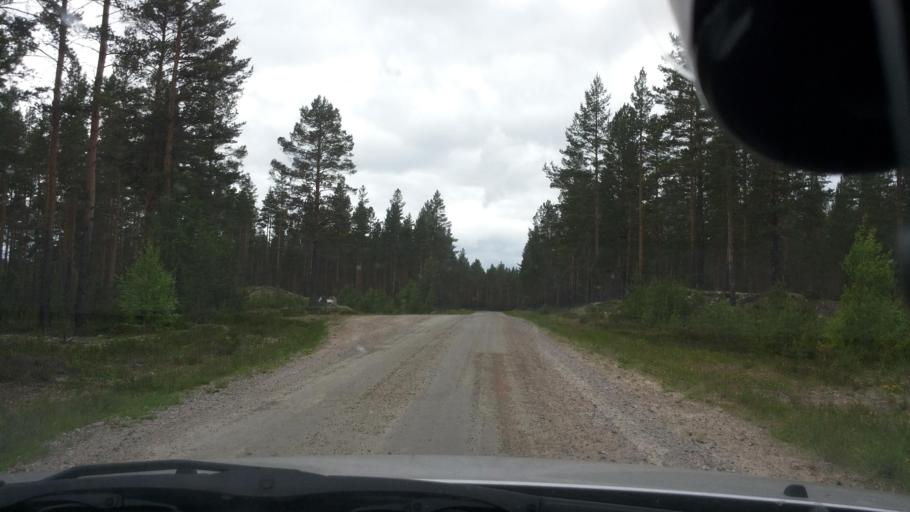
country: SE
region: Gaevleborg
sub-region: Ovanakers Kommun
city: Edsbyn
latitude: 61.5133
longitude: 15.3453
